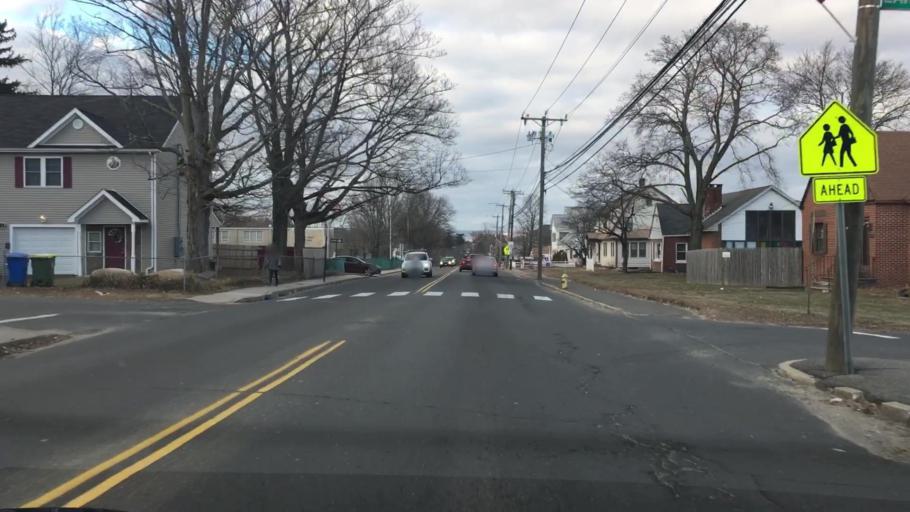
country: US
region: Connecticut
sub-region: New Haven County
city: Waterbury
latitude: 41.5448
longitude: -73.0555
